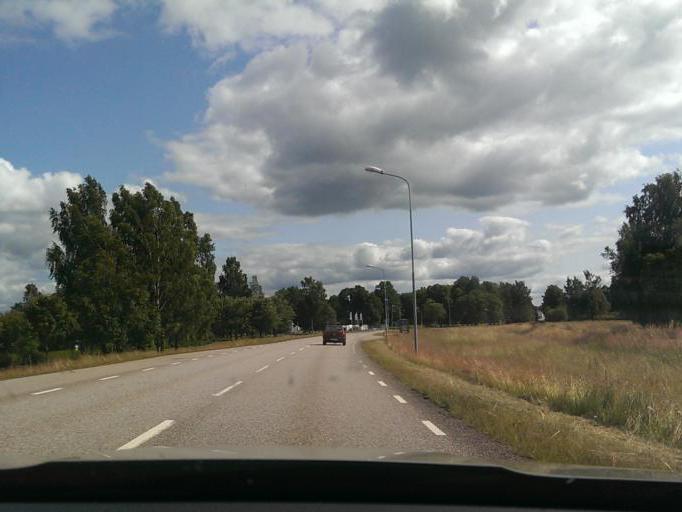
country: SE
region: Kronoberg
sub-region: Ljungby Kommun
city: Lagan
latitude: 56.9205
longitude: 13.9896
